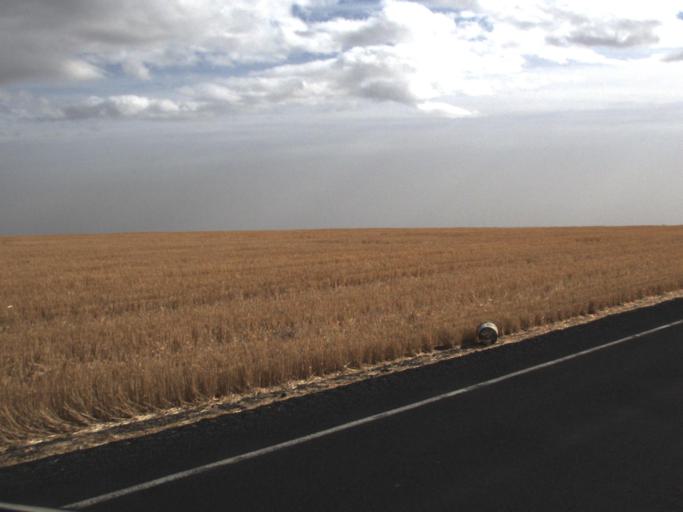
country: US
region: Washington
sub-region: Okanogan County
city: Coulee Dam
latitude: 47.5008
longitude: -118.7849
